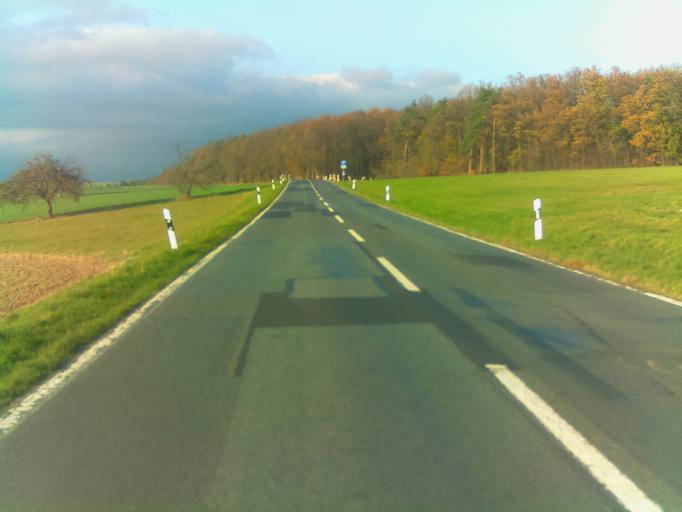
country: DE
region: Bavaria
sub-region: Regierungsbezirk Unterfranken
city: Eichenbuhl
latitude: 49.6940
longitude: 9.3587
